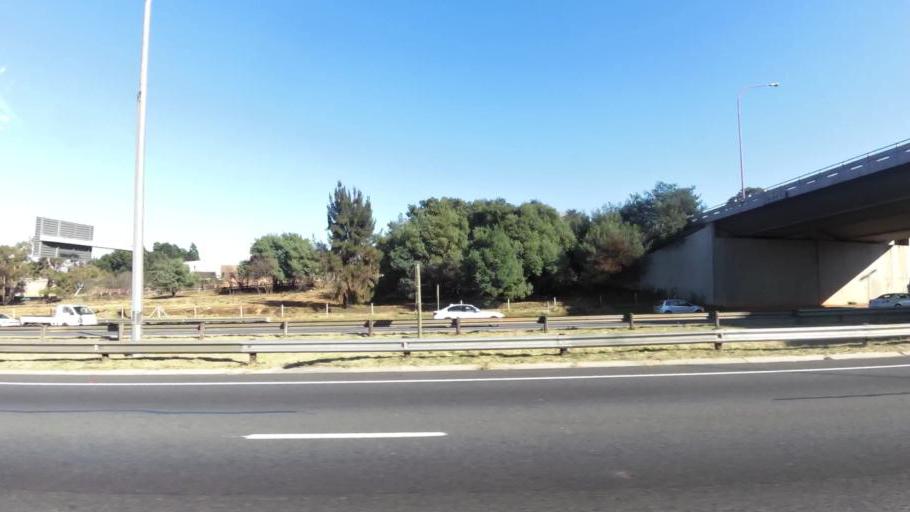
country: ZA
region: Gauteng
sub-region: City of Johannesburg Metropolitan Municipality
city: Roodepoort
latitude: -26.1792
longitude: 27.9457
